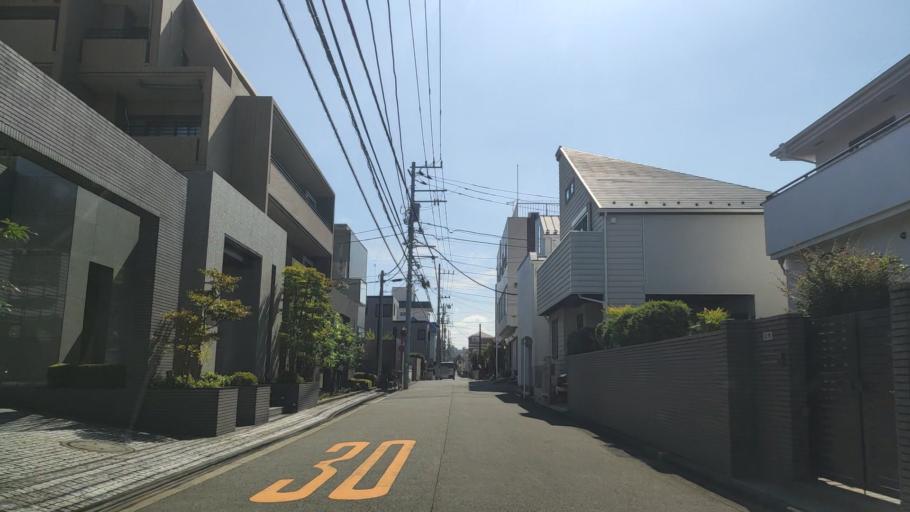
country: JP
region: Kanagawa
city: Yokohama
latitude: 35.5205
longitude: 139.6237
